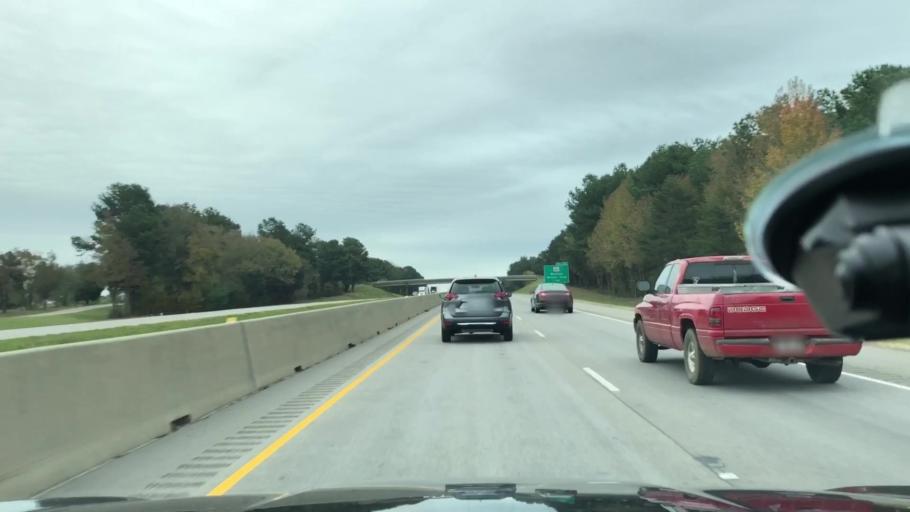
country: US
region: Texas
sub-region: Franklin County
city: Mount Vernon
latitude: 33.1614
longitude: -95.1356
